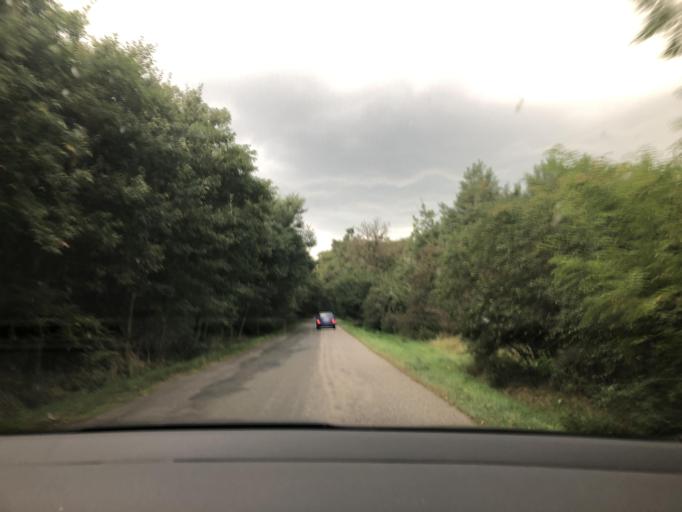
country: CZ
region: Central Bohemia
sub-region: Okres Kolin
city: Tynec nad Labem
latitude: 50.0511
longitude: 15.3761
